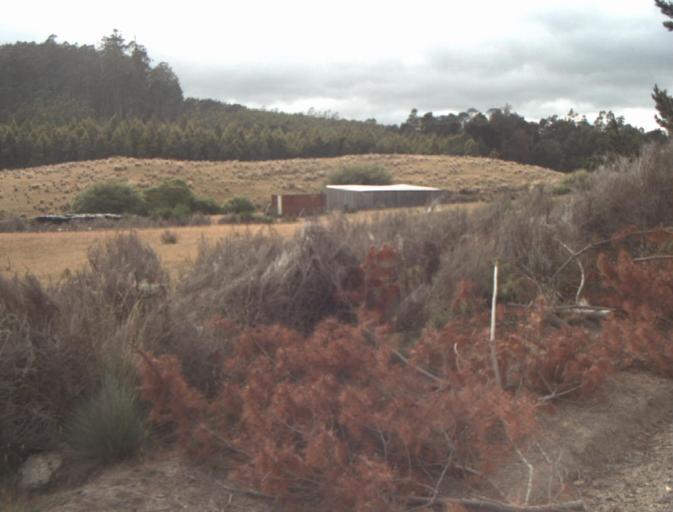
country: AU
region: Tasmania
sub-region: Dorset
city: Scottsdale
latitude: -41.3672
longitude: 147.4683
